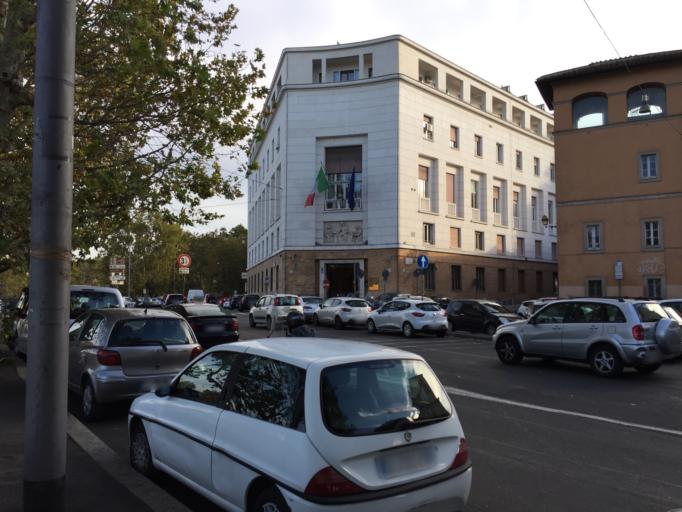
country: VA
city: Vatican City
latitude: 41.8895
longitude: 12.4777
